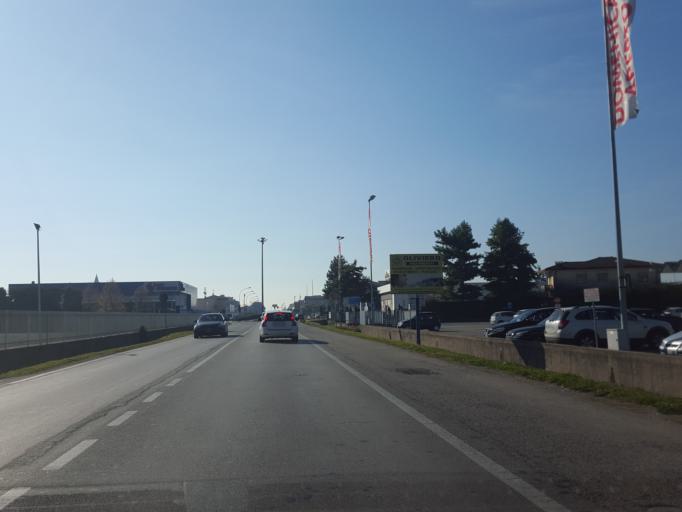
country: IT
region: Veneto
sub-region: Provincia di Vicenza
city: Tavernelle
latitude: 45.5014
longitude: 11.4373
